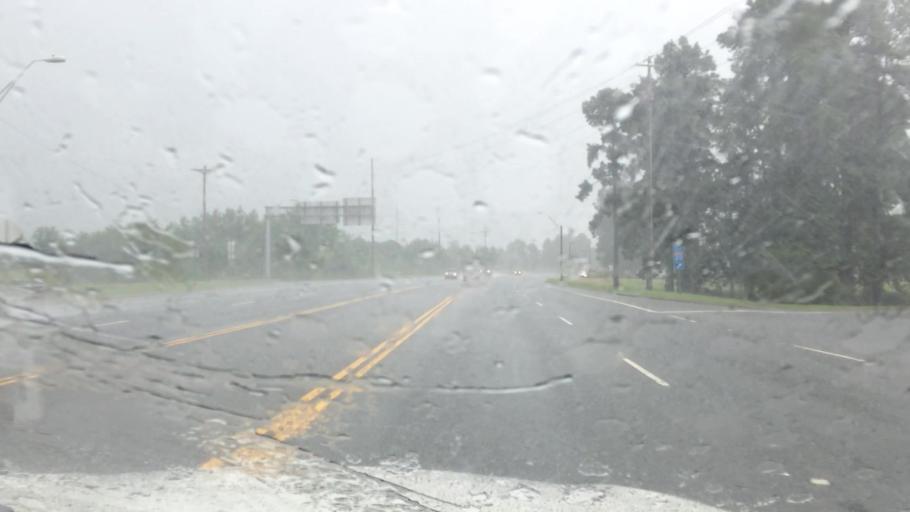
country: US
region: South Carolina
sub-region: Aiken County
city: North Augusta
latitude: 33.5394
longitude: -81.9911
